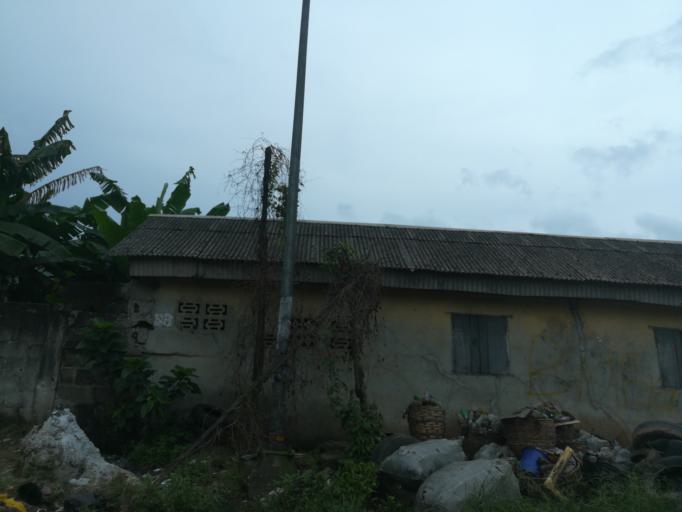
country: NG
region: Rivers
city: Port Harcourt
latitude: 4.7643
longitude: 7.0266
